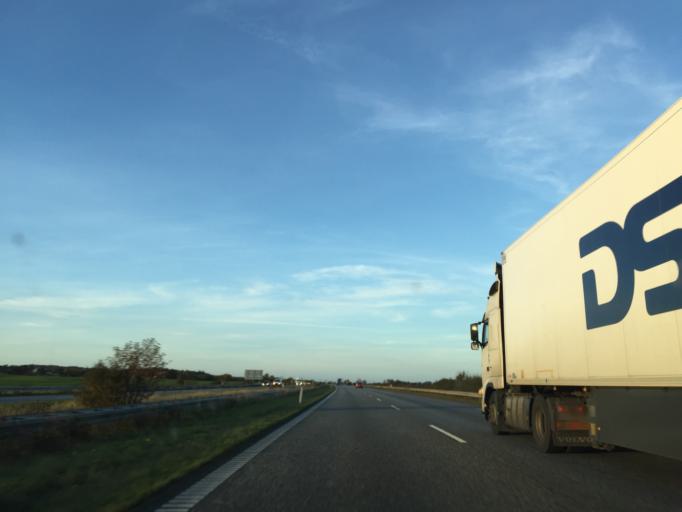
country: DK
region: South Denmark
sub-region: Kolding Kommune
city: Christiansfeld
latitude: 55.3718
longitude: 9.4514
